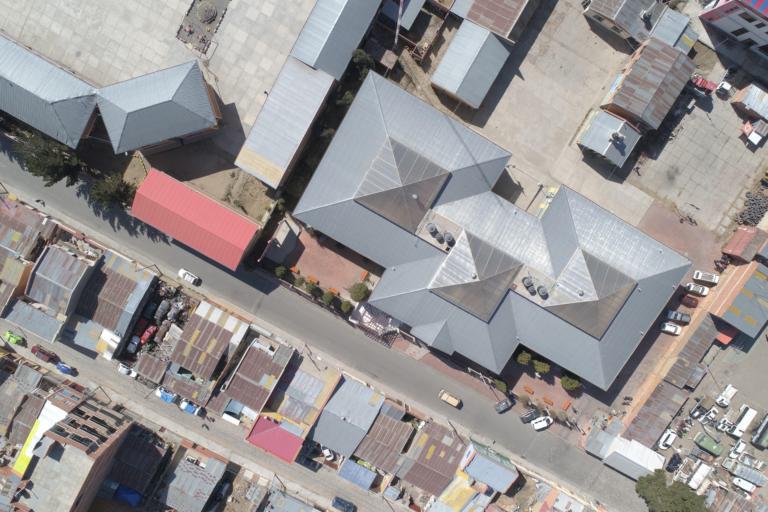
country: BO
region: La Paz
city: La Paz
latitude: -16.5275
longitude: -68.1526
